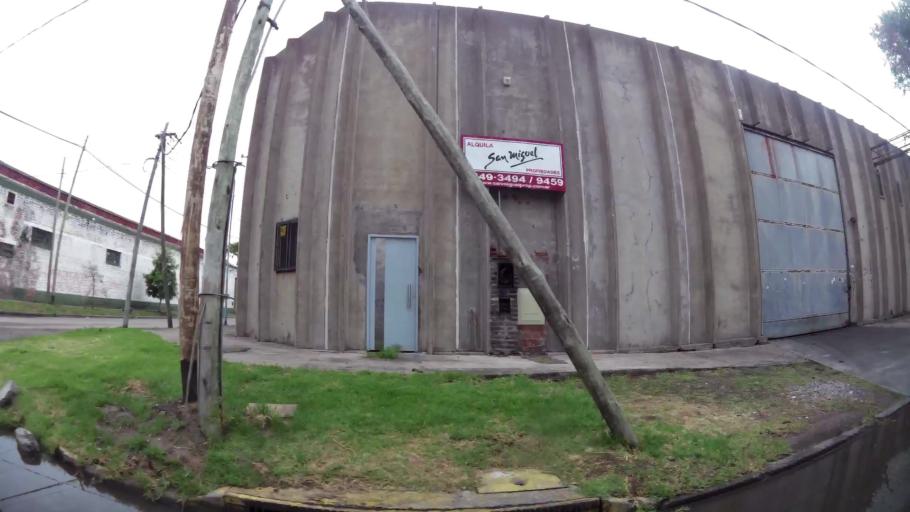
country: AR
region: Buenos Aires
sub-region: Partido de Lanus
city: Lanus
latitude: -34.7101
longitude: -58.3605
